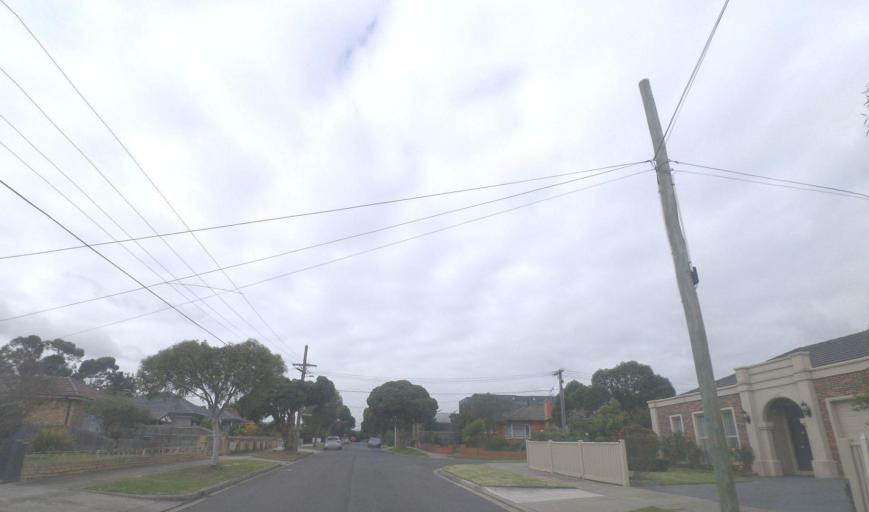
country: AU
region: Victoria
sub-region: Whitehorse
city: Box Hill North
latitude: -37.7983
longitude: 145.1315
